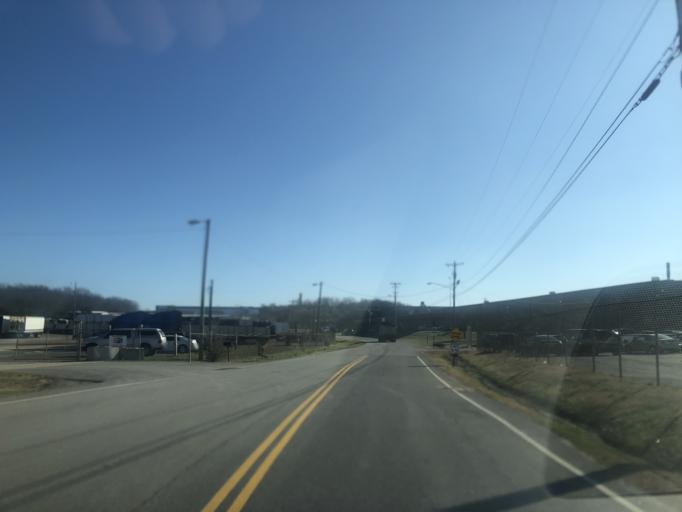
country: US
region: Tennessee
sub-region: Rutherford County
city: La Vergne
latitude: 36.0073
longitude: -86.5944
